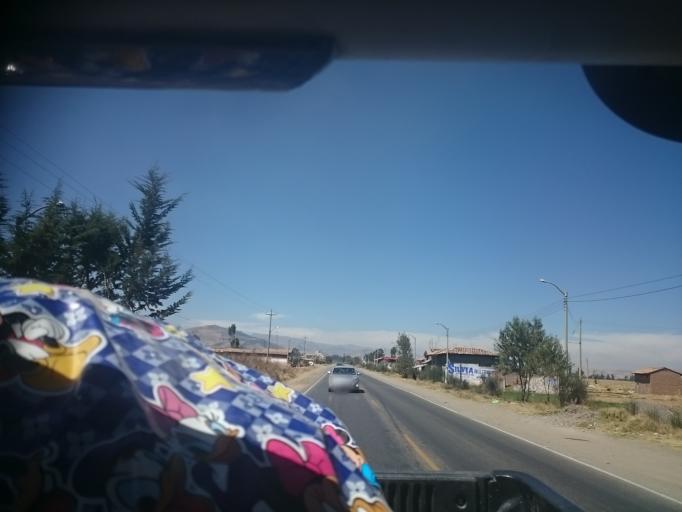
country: PE
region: Junin
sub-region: Provincia de Jauja
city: San Lorenzo
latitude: -11.8286
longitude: -75.4040
